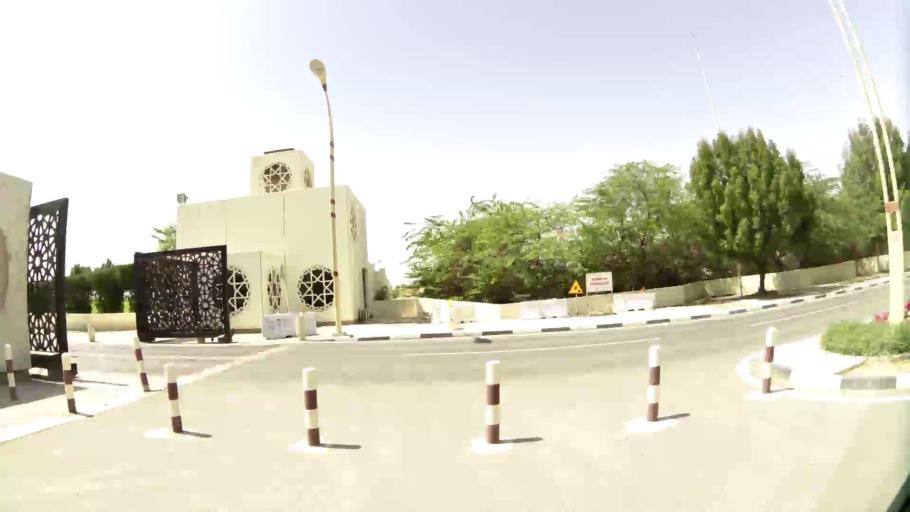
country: QA
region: Baladiyat ad Dawhah
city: Doha
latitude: 25.3669
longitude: 51.4955
